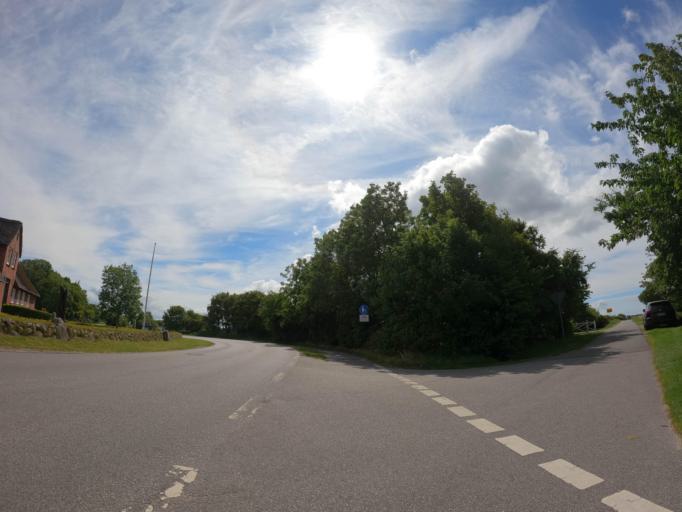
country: DE
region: Schleswig-Holstein
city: Sylt-Ost
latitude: 54.8697
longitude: 8.4390
